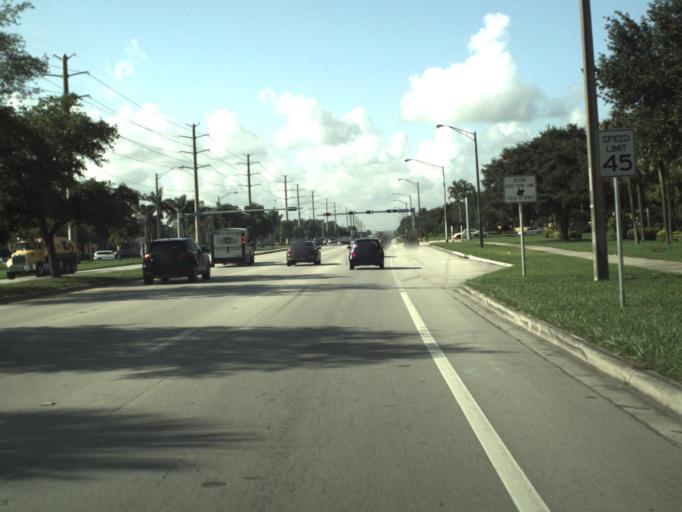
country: US
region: Florida
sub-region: Broward County
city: Parkland
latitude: 26.2948
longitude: -80.2022
